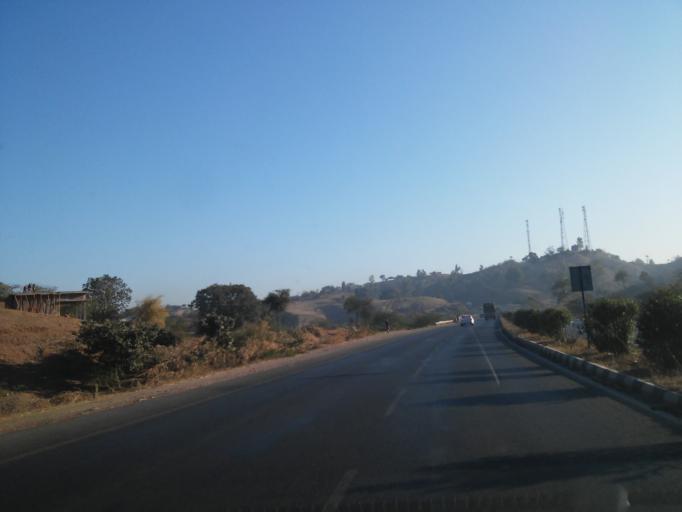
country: IN
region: Rajasthan
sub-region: Dungarpur
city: Dungarpur
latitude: 23.8888
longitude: 73.5368
